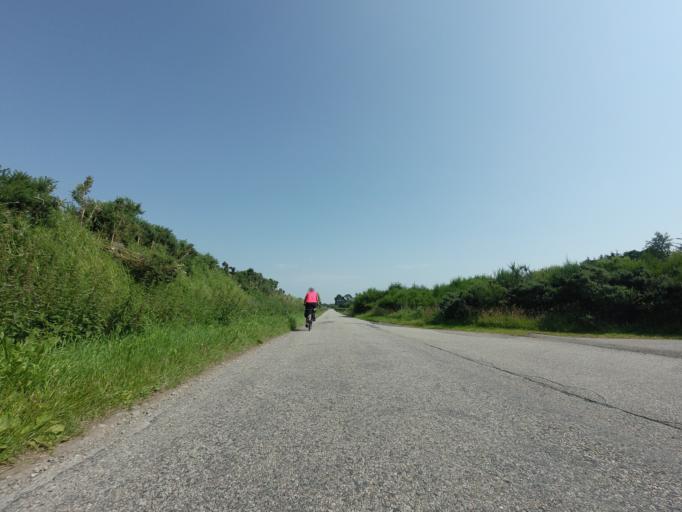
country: GB
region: Scotland
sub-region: Highland
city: Tain
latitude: 57.7971
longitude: -4.0720
